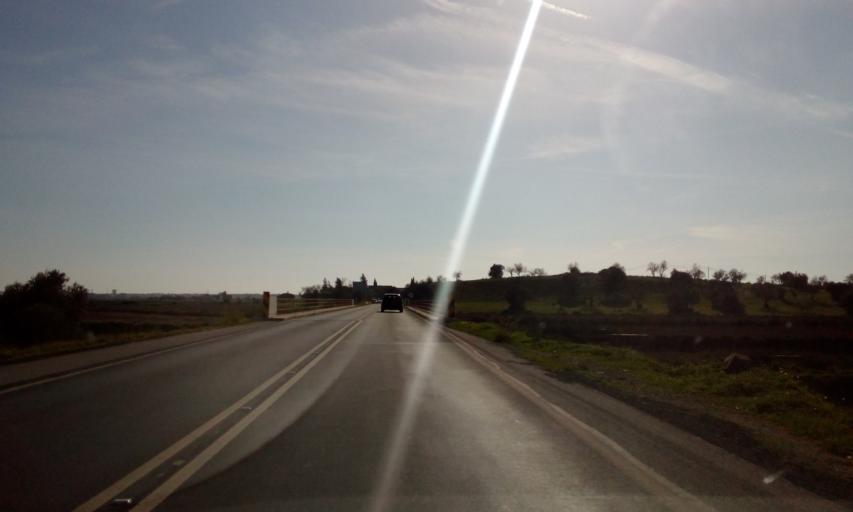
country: PT
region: Faro
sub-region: Castro Marim
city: Castro Marim
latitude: 37.2143
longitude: -7.4385
